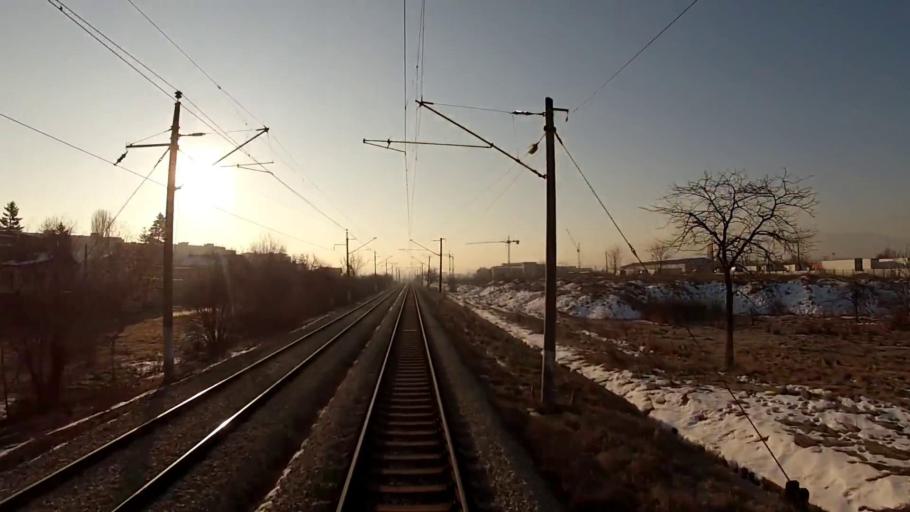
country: BG
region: Sofiya
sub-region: Obshtina Bozhurishte
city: Bozhurishte
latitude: 42.7464
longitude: 23.2549
